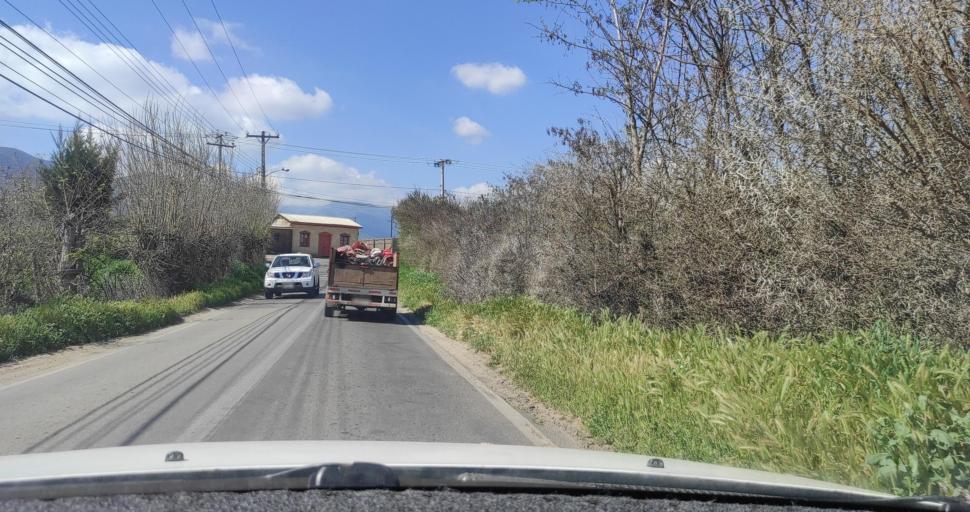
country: CL
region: Valparaiso
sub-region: Provincia de Marga Marga
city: Limache
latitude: -33.0016
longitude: -71.2339
